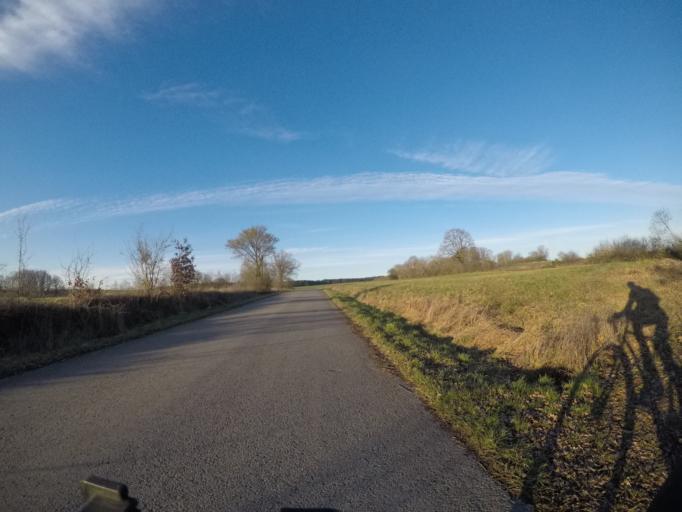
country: BE
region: Wallonia
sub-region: Province du Luxembourg
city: Habay-la-Vieille
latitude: 49.7238
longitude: 5.5937
